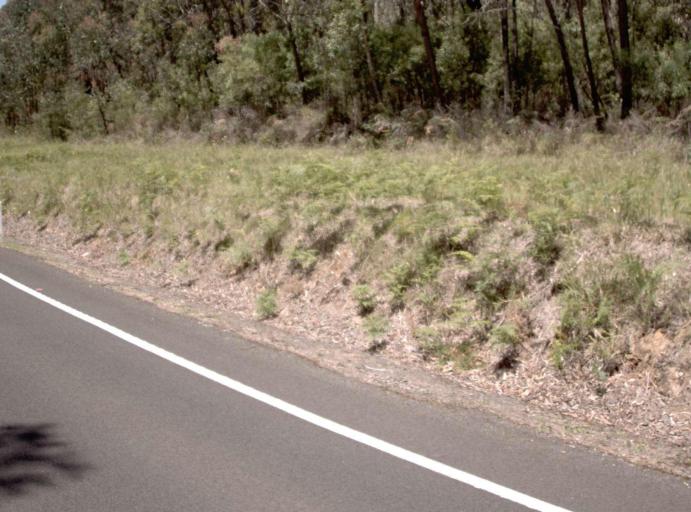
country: AU
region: Victoria
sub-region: East Gippsland
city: Lakes Entrance
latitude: -37.6952
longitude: 148.5911
